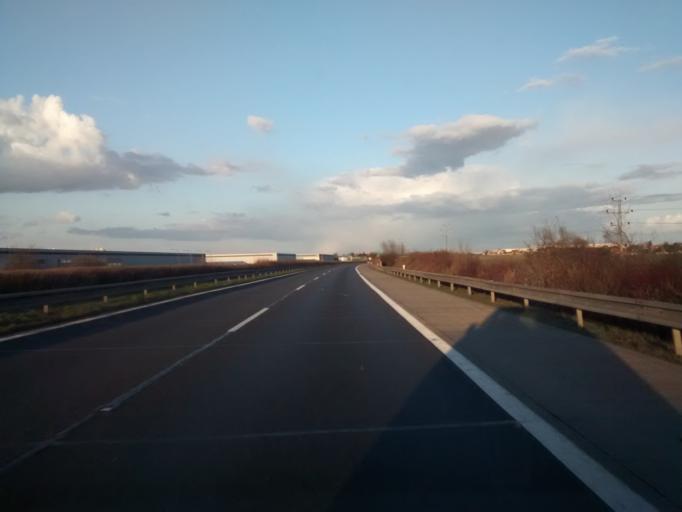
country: CZ
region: Central Bohemia
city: Sestajovice
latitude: 50.1212
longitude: 14.6850
